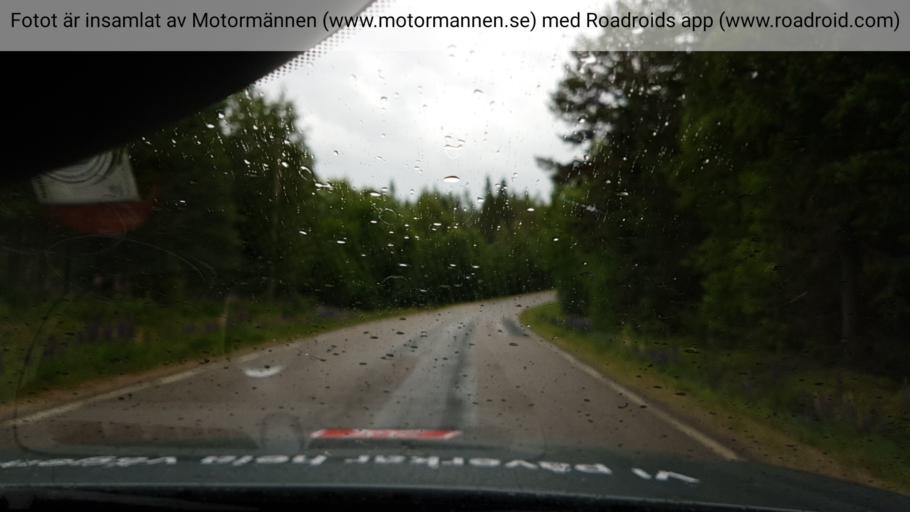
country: SE
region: Jaemtland
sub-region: Braecke Kommun
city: Braecke
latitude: 62.3792
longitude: 15.1698
